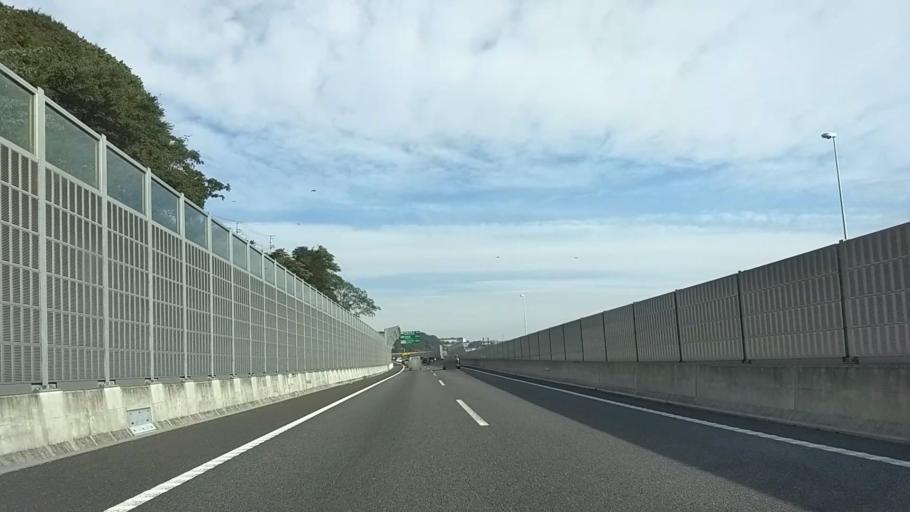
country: JP
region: Kanagawa
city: Zama
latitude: 35.4933
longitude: 139.3680
